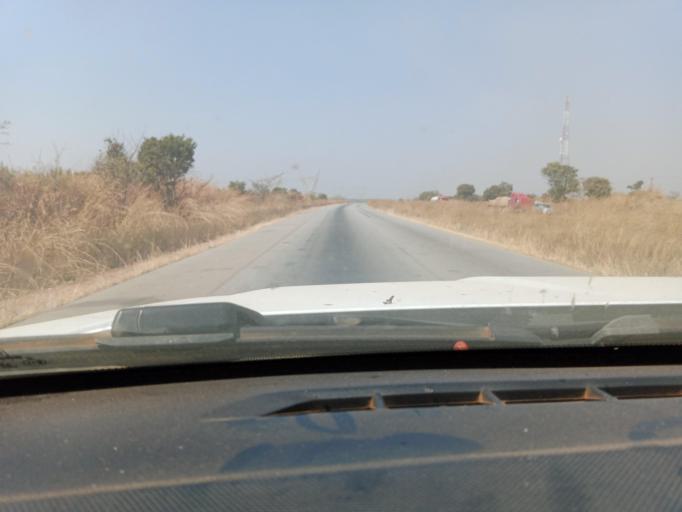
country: ZM
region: Copperbelt
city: Luanshya
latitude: -12.9483
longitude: 28.3812
